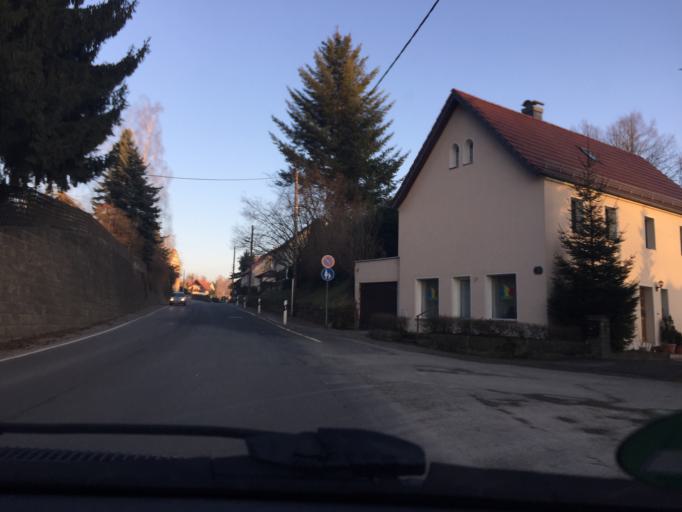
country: DE
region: Saxony
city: Struppen
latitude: 50.9359
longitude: 14.0063
